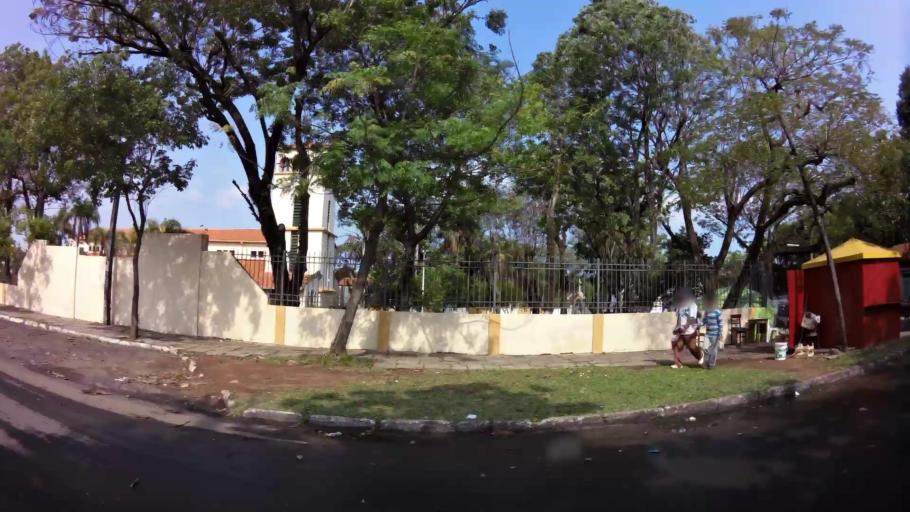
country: PY
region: Presidente Hayes
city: Nanawa
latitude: -25.2937
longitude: -57.6662
